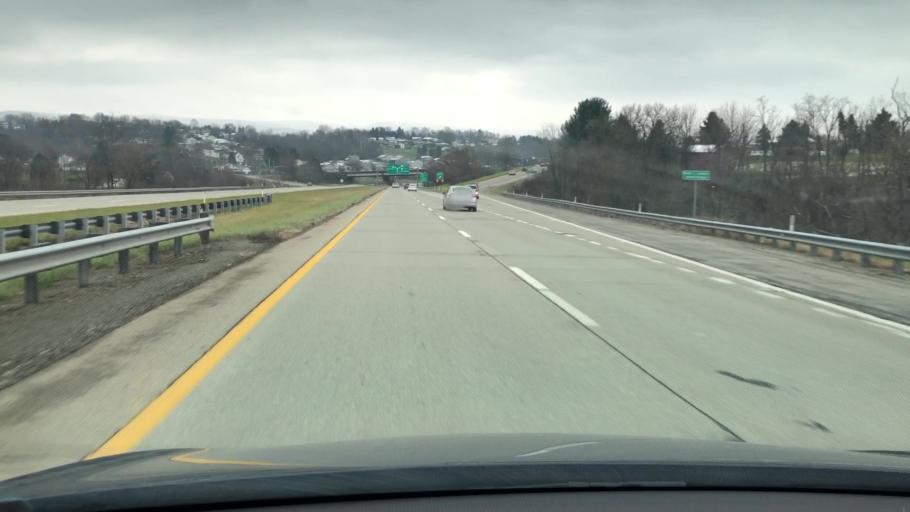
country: US
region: Pennsylvania
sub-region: Fayette County
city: South Uniontown
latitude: 39.8854
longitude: -79.7487
